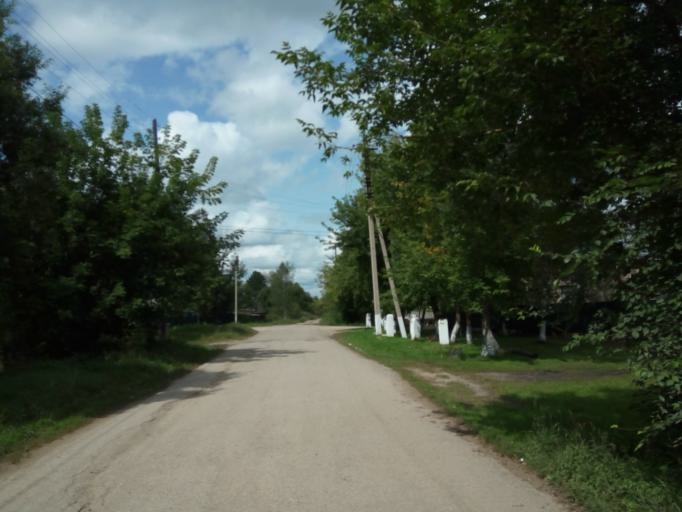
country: RU
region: Primorskiy
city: Dal'nerechensk
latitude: 45.9514
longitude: 133.8084
